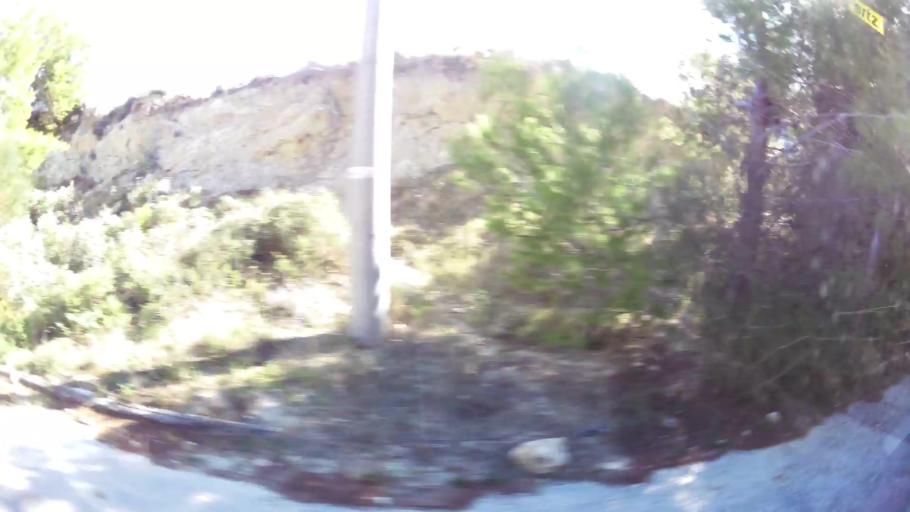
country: GR
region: Attica
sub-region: Nomarchia Anatolikis Attikis
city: Dhrafi
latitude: 38.0192
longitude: 23.9168
